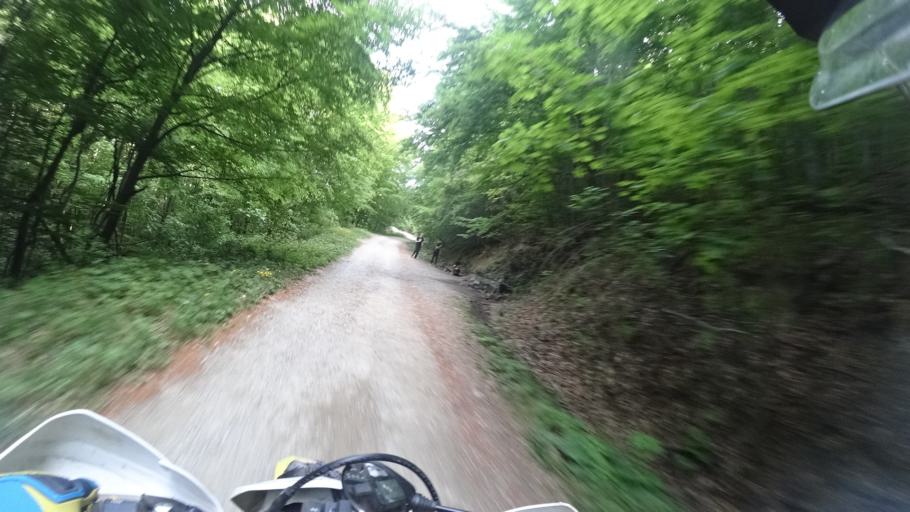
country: HR
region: Zagrebacka
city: Jablanovec
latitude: 45.8582
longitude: 15.8896
